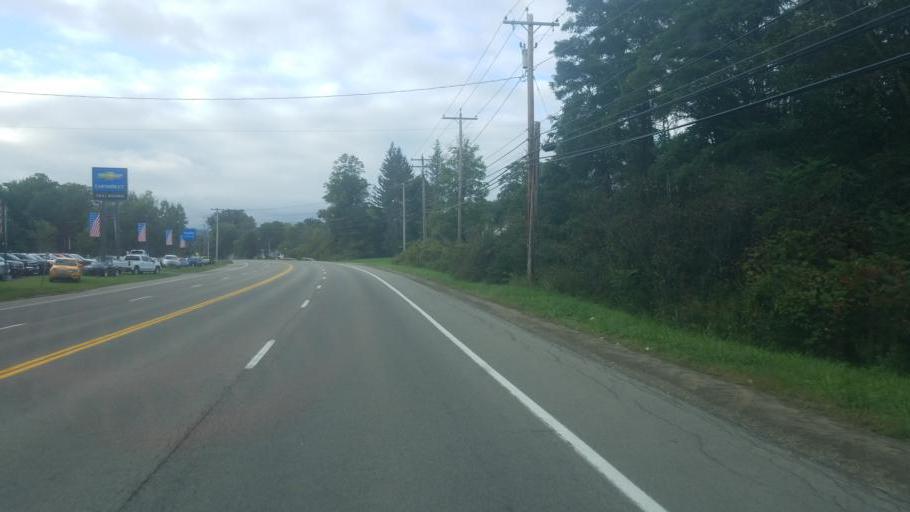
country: US
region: New York
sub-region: Cattaraugus County
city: Olean
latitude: 42.1226
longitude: -78.4144
